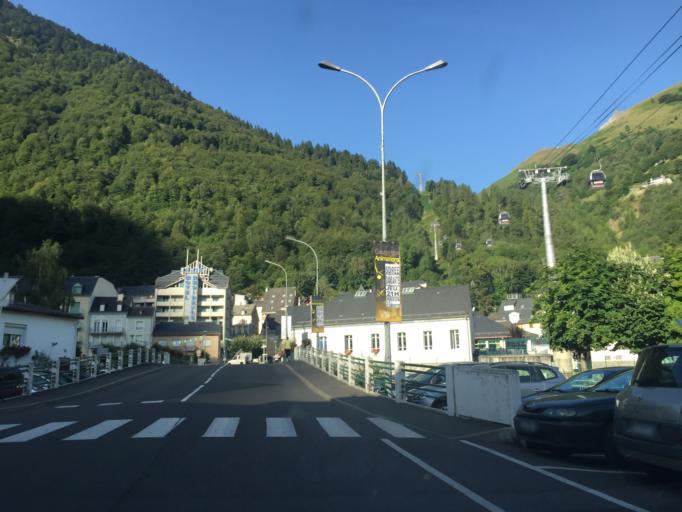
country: FR
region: Midi-Pyrenees
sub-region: Departement des Hautes-Pyrenees
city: Cauterets
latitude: 42.8908
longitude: -0.1141
